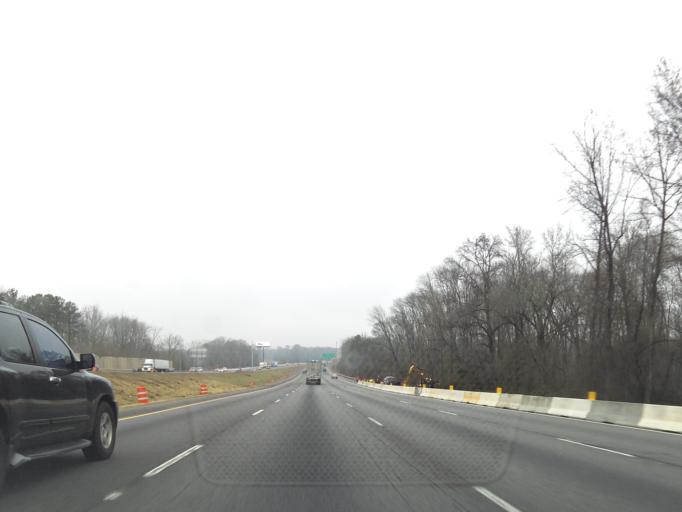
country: US
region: Georgia
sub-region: Henry County
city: Stockbridge
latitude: 33.5127
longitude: -84.2387
